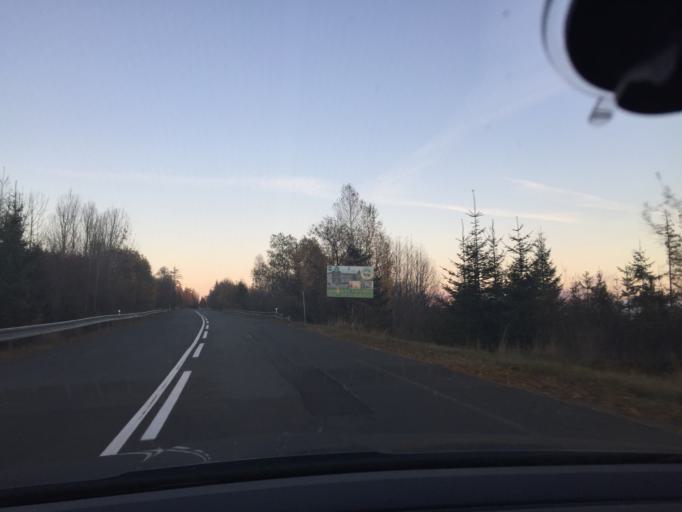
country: SK
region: Presovsky
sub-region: Okres Poprad
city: Svit
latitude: 49.1214
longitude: 20.1765
